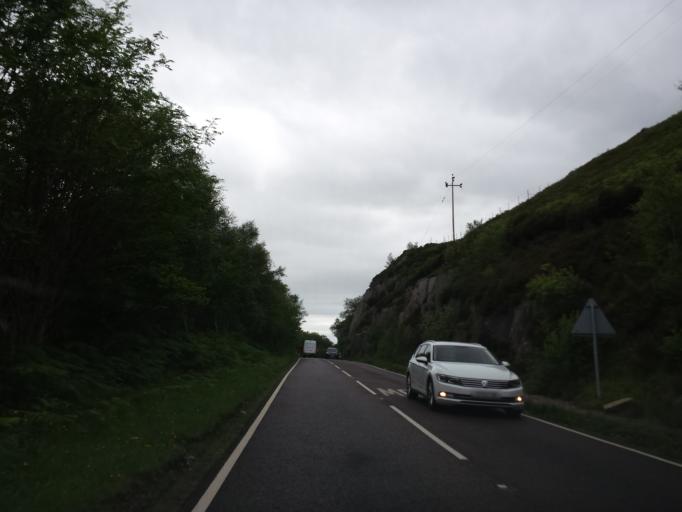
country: GB
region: Scotland
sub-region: Argyll and Bute
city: Isle Of Mull
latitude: 56.8834
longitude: -5.6047
